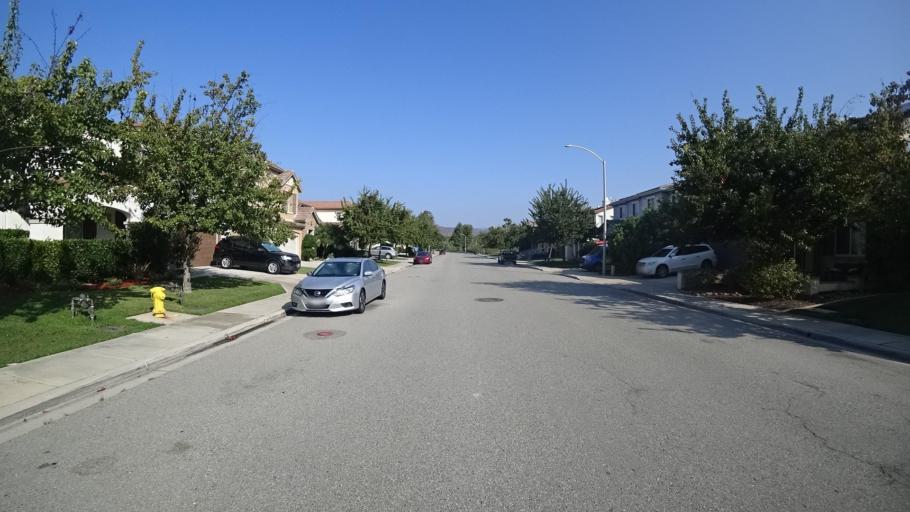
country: US
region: California
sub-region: San Diego County
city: Bonsall
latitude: 33.3224
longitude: -117.1553
